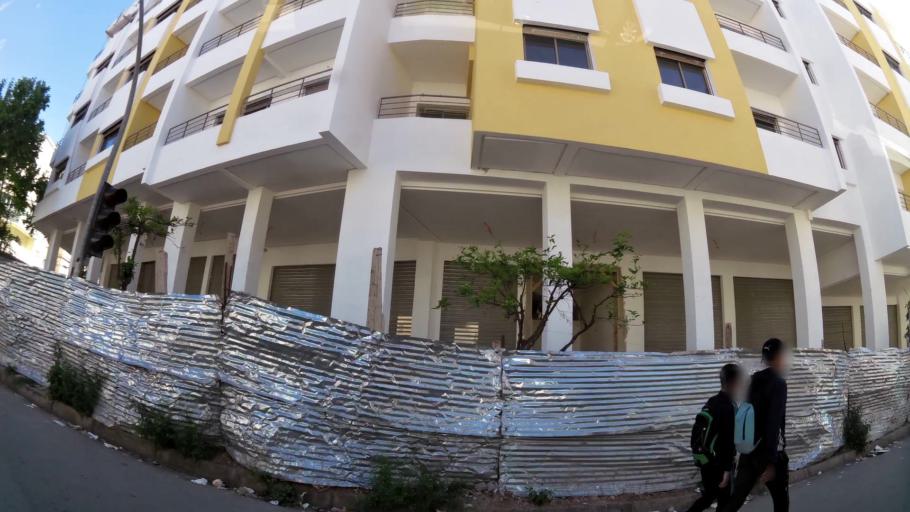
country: MA
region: Fes-Boulemane
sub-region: Fes
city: Fes
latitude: 34.0182
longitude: -4.9818
